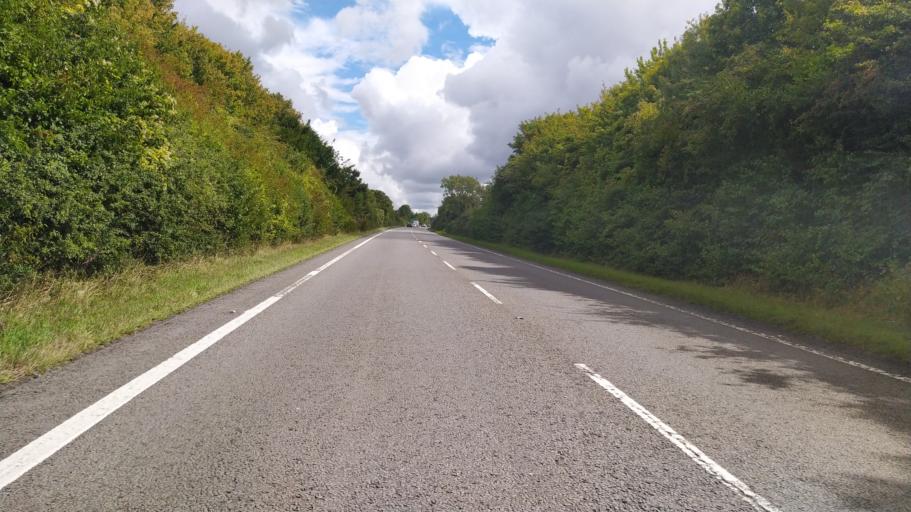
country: GB
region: England
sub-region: Dorset
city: Blandford Forum
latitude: 50.8735
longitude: -2.1650
